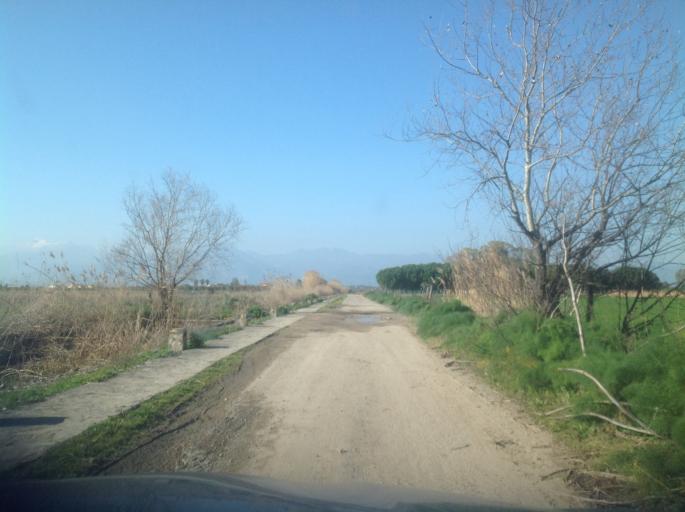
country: IT
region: Calabria
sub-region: Provincia di Cosenza
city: Sibari
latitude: 39.7200
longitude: 16.4963
